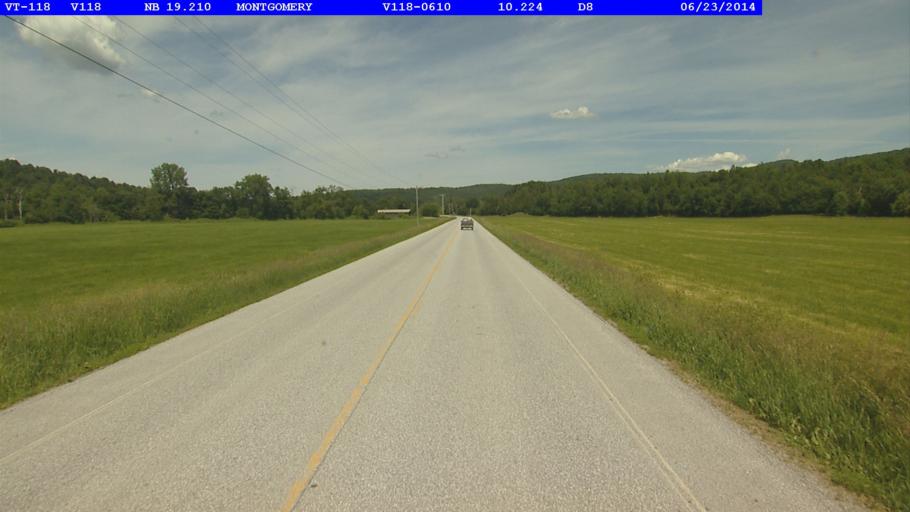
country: US
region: Vermont
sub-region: Franklin County
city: Richford
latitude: 44.9172
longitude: -72.6698
